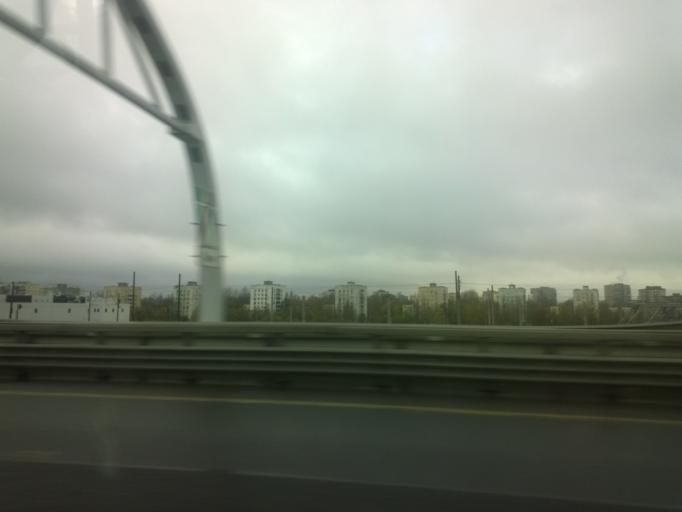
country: RU
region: St.-Petersburg
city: Dachnoye
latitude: 59.8452
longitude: 30.2855
